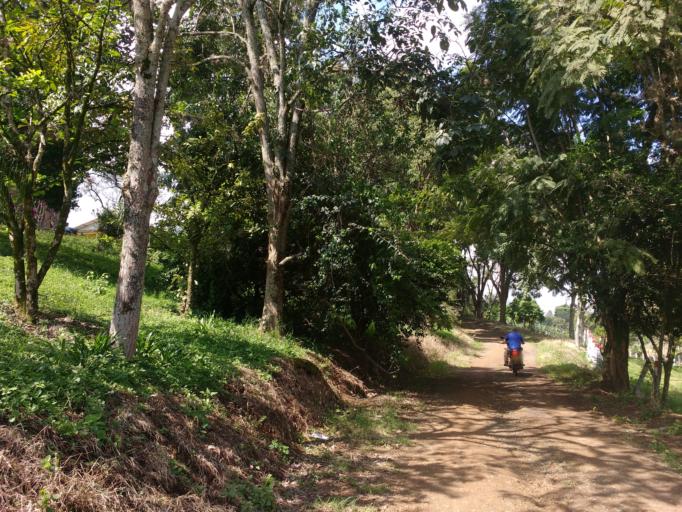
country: CO
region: Cauca
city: Santander de Quilichao
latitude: 2.9831
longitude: -76.4532
